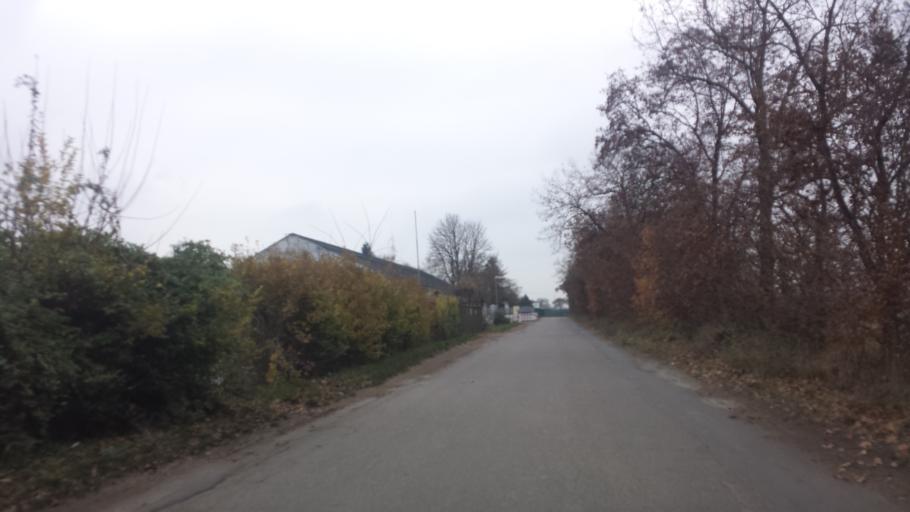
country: DE
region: Hesse
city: Lampertheim
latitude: 49.6191
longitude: 8.4779
